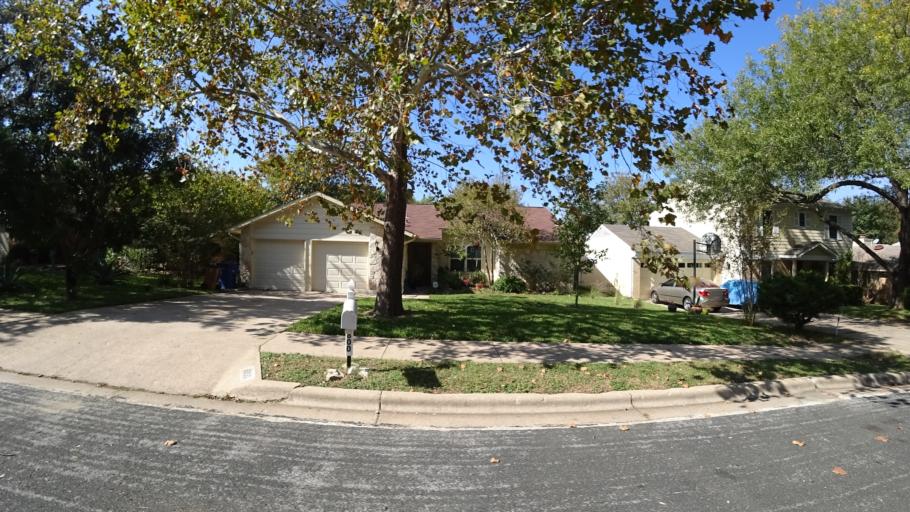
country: US
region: Texas
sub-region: Travis County
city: Shady Hollow
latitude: 30.2128
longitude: -97.8235
